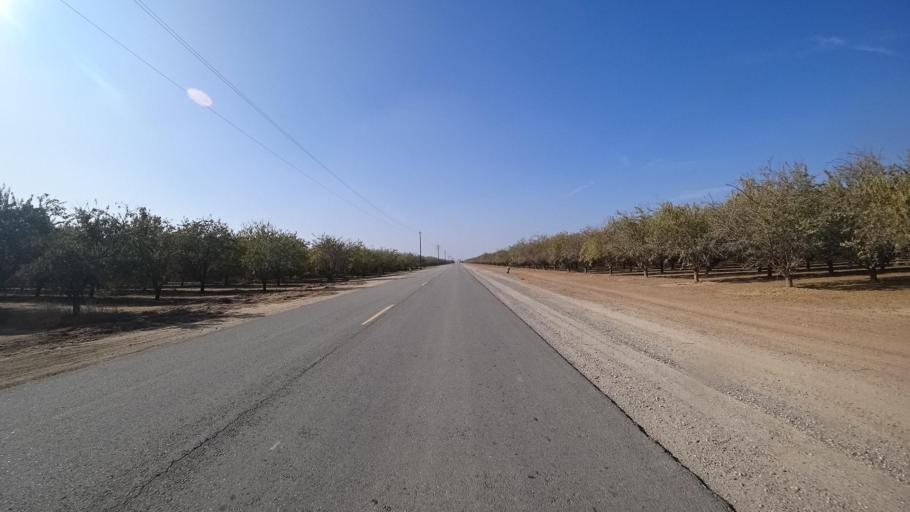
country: US
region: California
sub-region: Kern County
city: Shafter
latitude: 35.5297
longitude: -119.1615
